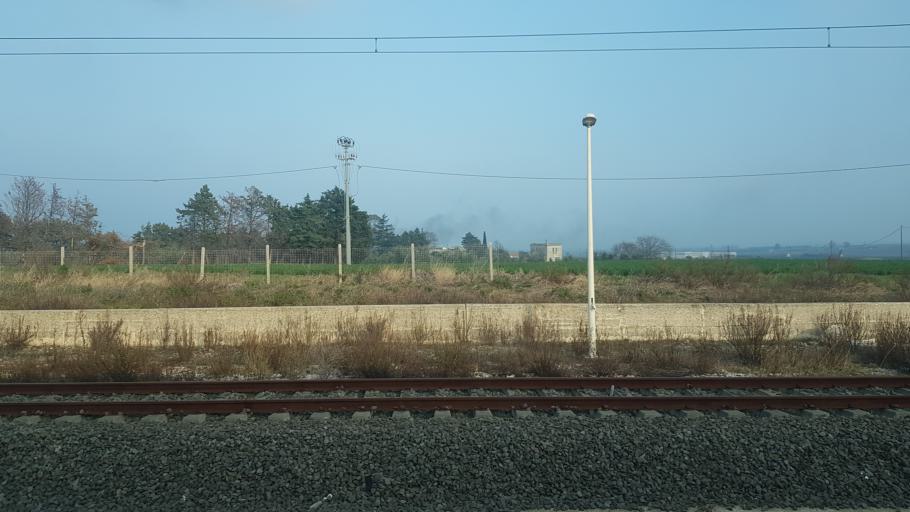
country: IT
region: Apulia
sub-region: Provincia di Foggia
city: Lesina
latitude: 41.8551
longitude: 15.2962
